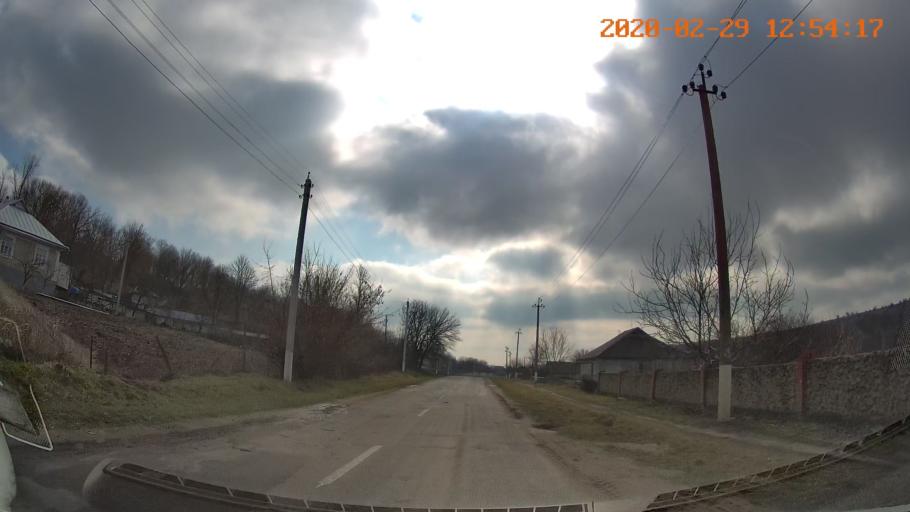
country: MD
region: Telenesti
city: Camenca
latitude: 48.1031
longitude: 28.7278
